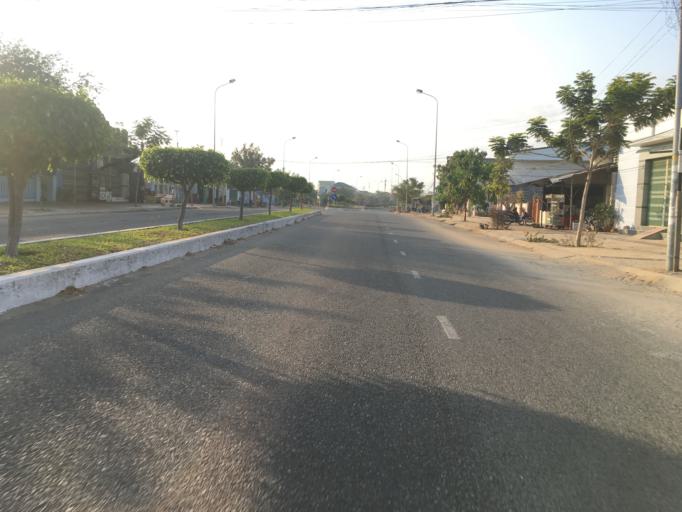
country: VN
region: Ninh Thuan
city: Phan Rang-Thap Cham
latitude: 11.5550
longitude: 109.0235
